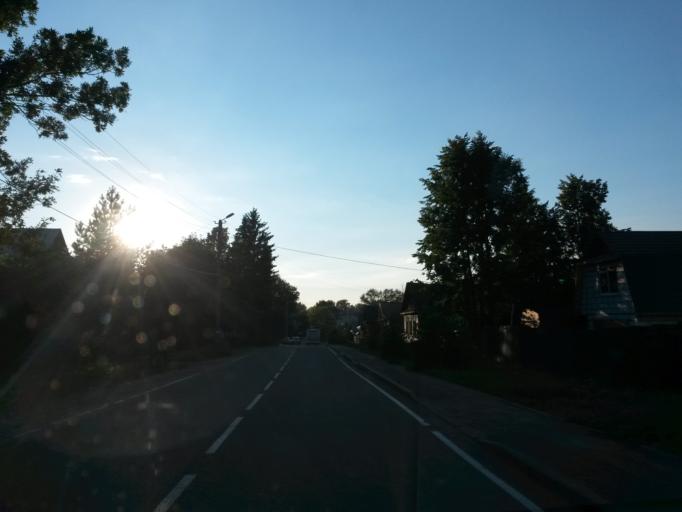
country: RU
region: Jaroslavl
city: Tutayev
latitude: 57.8735
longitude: 39.5240
